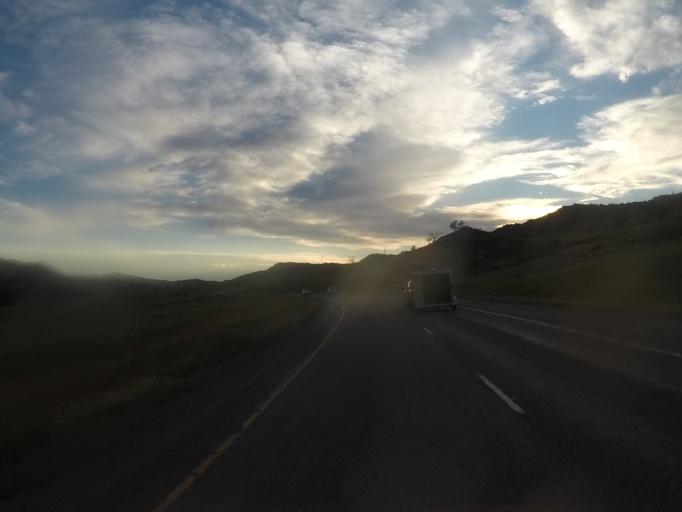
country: US
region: Montana
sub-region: Park County
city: Livingston
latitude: 45.6644
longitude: -110.6834
